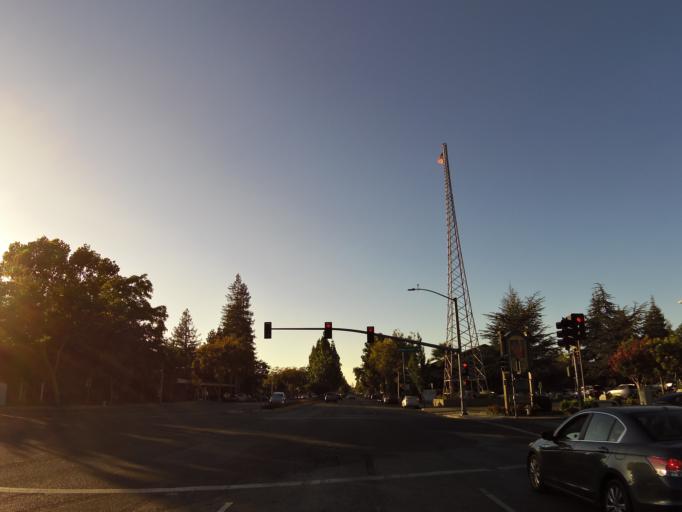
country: US
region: California
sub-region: Santa Clara County
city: Los Altos
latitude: 37.4066
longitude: -122.1201
